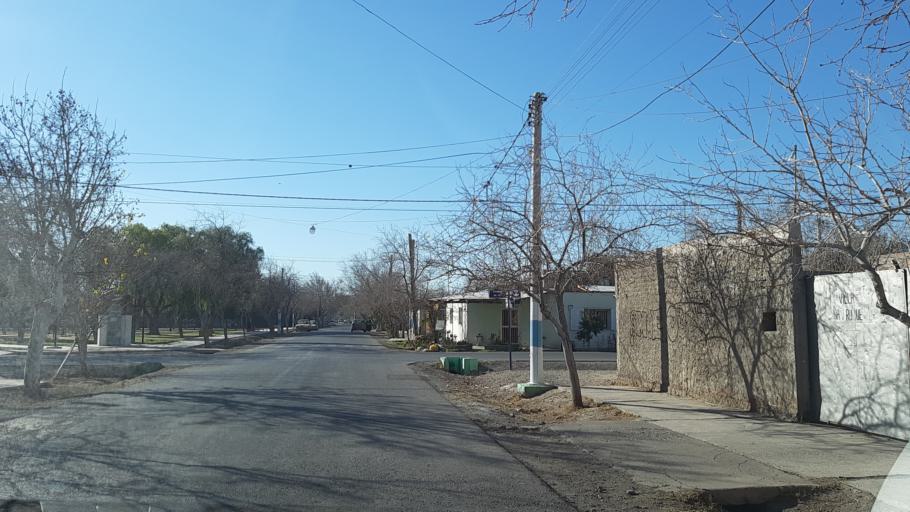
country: AR
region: San Juan
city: San Juan
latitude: -31.5378
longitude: -68.5760
